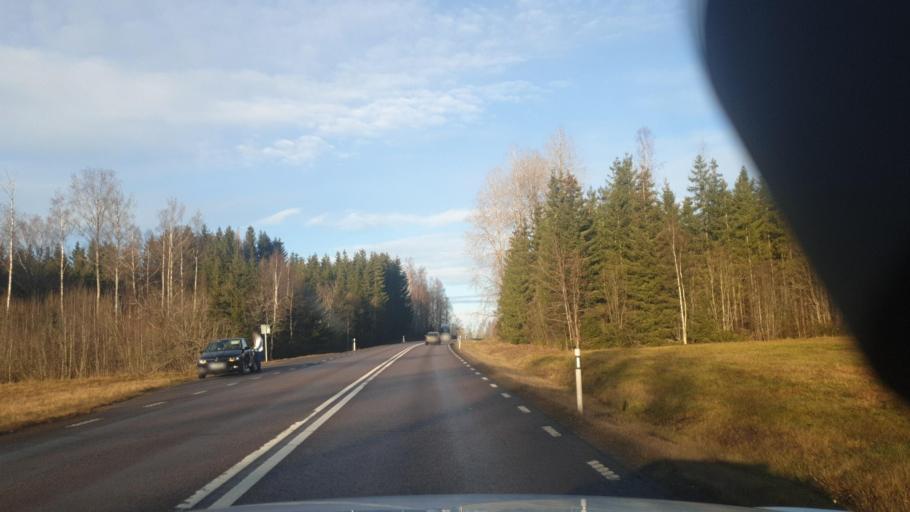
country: SE
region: Vaermland
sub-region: Karlstads Kommun
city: Edsvalla
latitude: 59.5665
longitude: 13.0246
